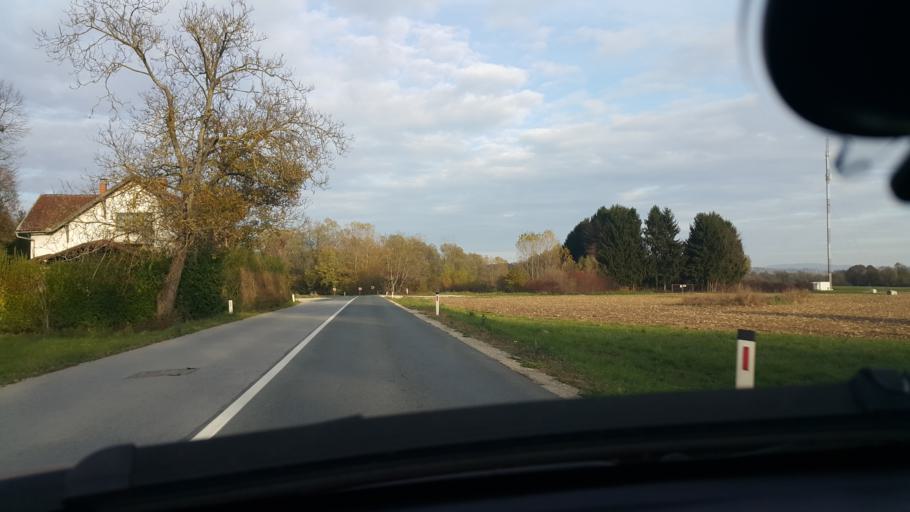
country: SI
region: Brezice
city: Brezice
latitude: 45.9084
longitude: 15.6120
